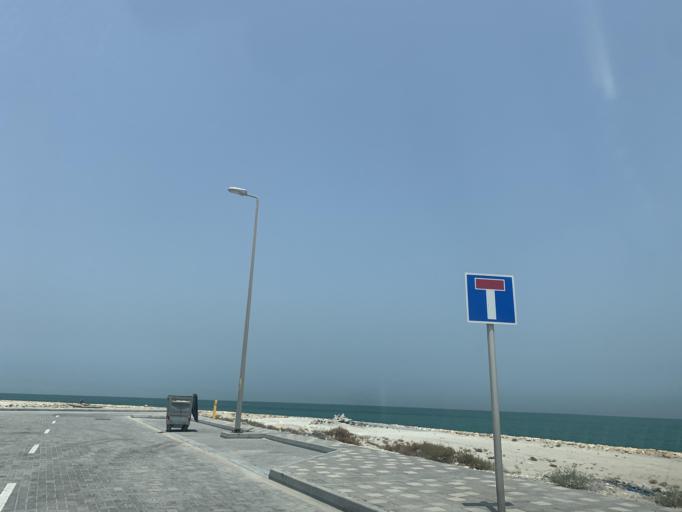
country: BH
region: Muharraq
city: Al Hadd
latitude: 26.2688
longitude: 50.6798
